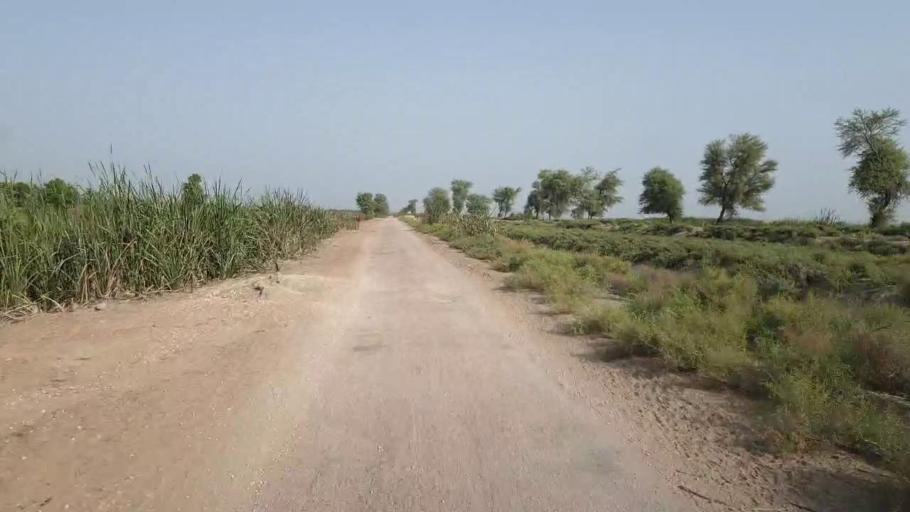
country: PK
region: Sindh
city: Daur
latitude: 26.3380
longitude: 68.1842
